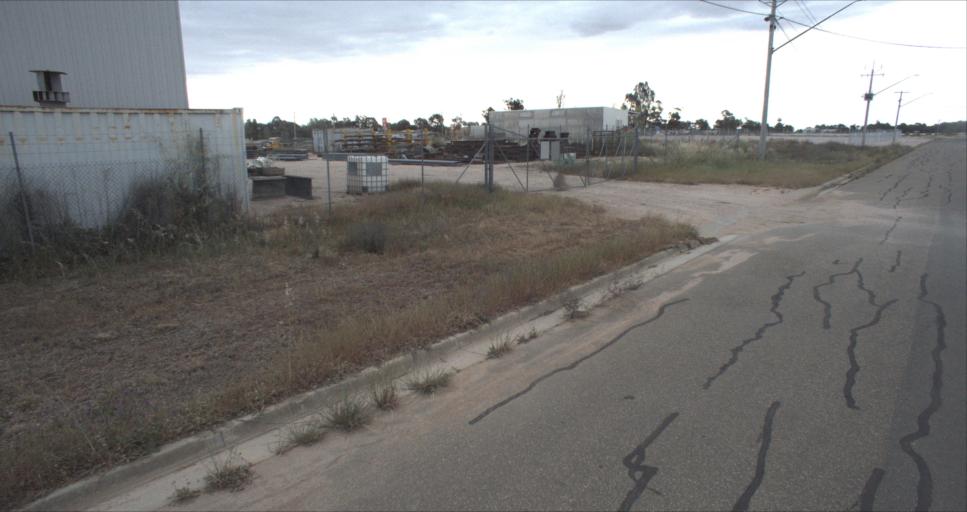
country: AU
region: New South Wales
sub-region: Leeton
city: Leeton
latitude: -34.5451
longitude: 146.3880
